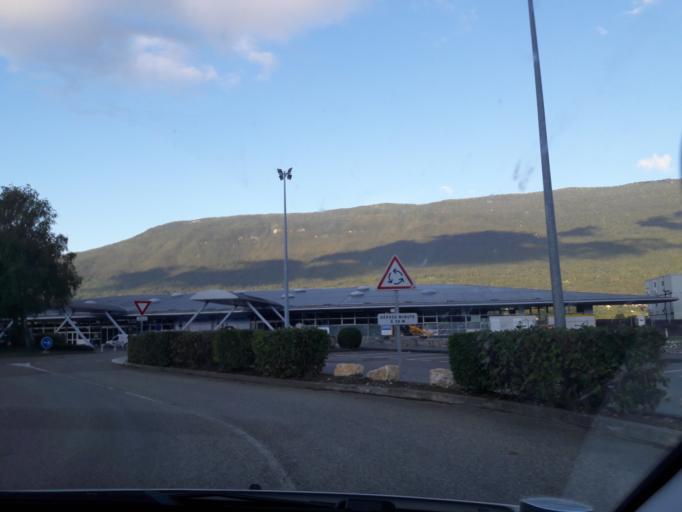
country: FR
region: Rhone-Alpes
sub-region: Departement de la Savoie
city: Voglans
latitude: 45.6383
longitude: 5.8850
